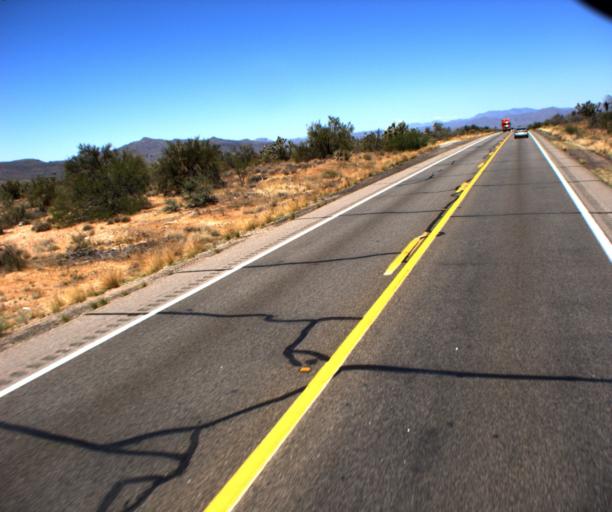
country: US
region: Arizona
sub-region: Yavapai County
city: Congress
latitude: 34.2629
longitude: -113.0894
